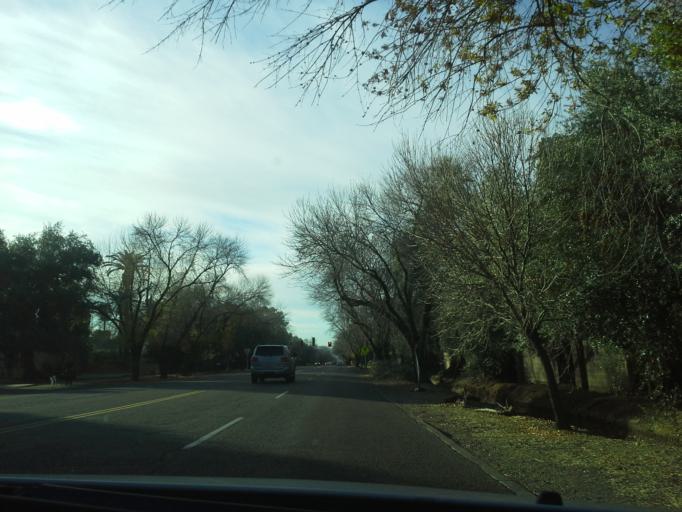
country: US
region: Arizona
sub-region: Maricopa County
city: Phoenix
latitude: 33.5401
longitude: -112.0738
